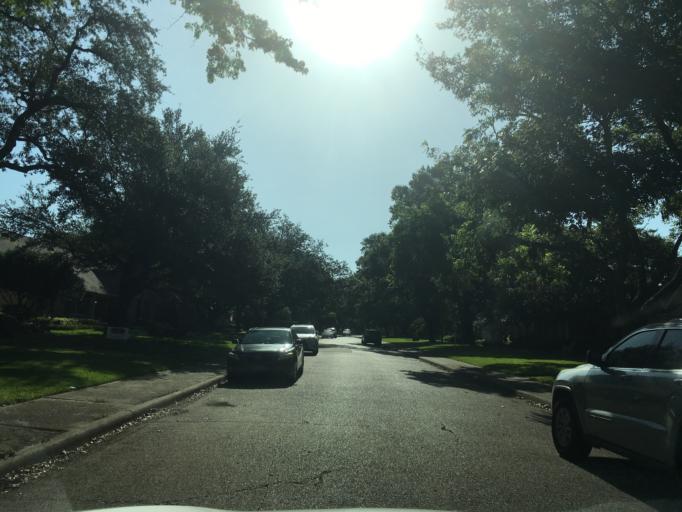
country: US
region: Texas
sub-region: Dallas County
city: Richardson
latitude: 32.8838
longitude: -96.7249
